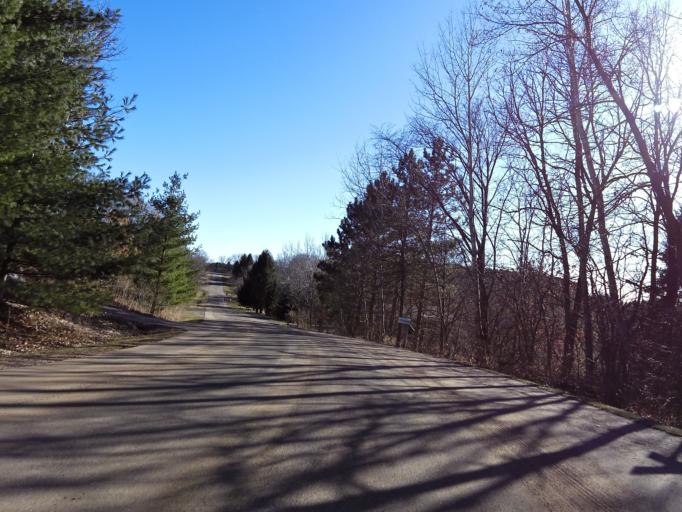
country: US
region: Minnesota
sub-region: Washington County
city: Lake Elmo
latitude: 44.9818
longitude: -92.8263
